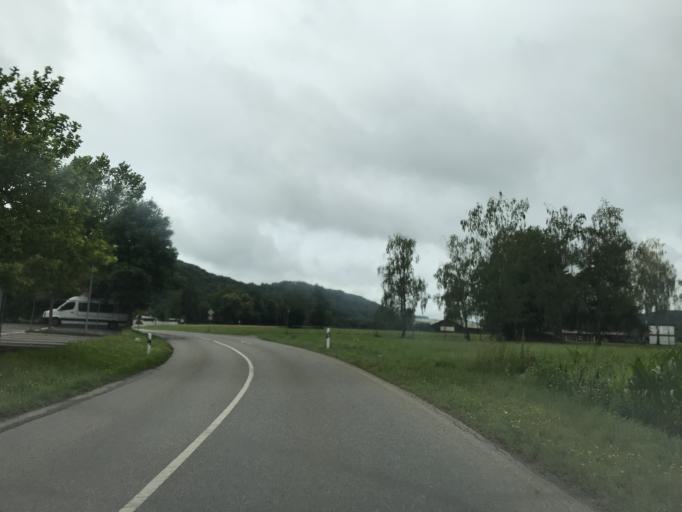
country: DE
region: Baden-Wuerttemberg
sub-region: Freiburg Region
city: Steinen
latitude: 47.6432
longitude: 7.7273
